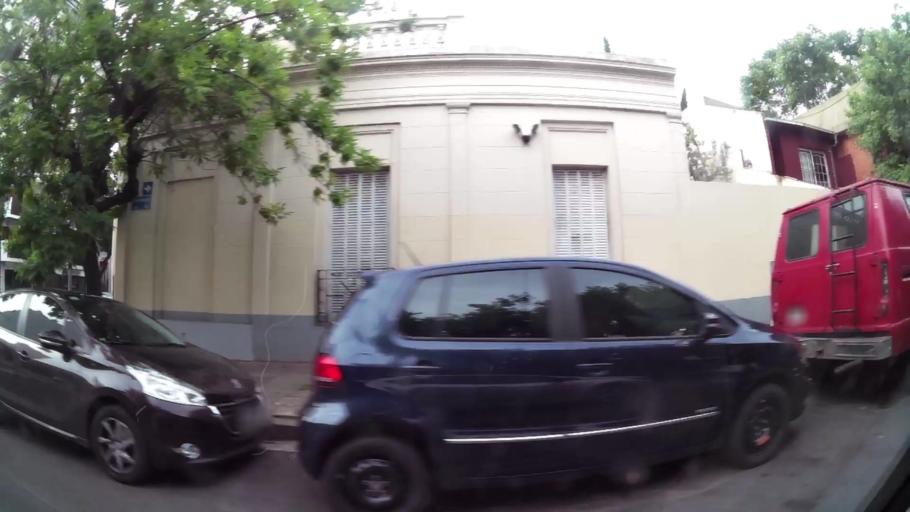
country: AR
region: Buenos Aires F.D.
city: Buenos Aires
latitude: -34.6292
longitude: -58.4248
